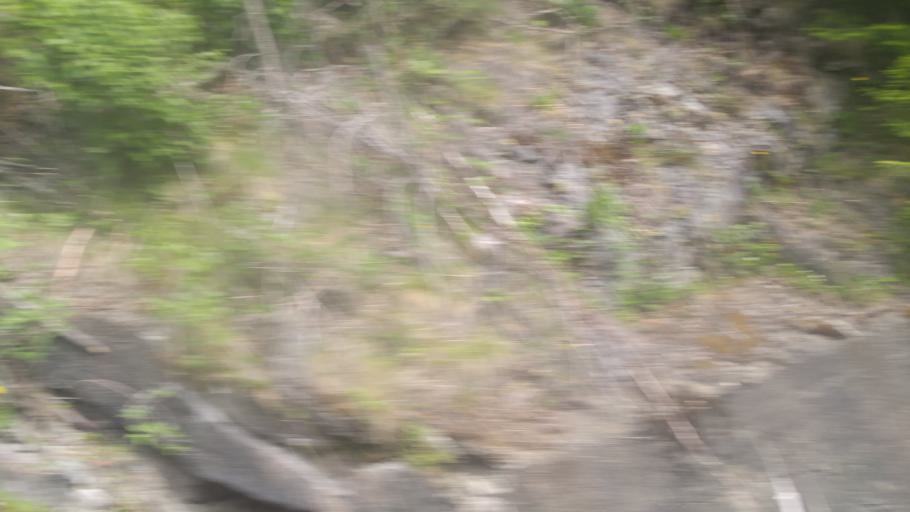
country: NO
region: Sor-Trondelag
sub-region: Selbu
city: Mebonden
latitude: 62.9662
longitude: 10.9602
